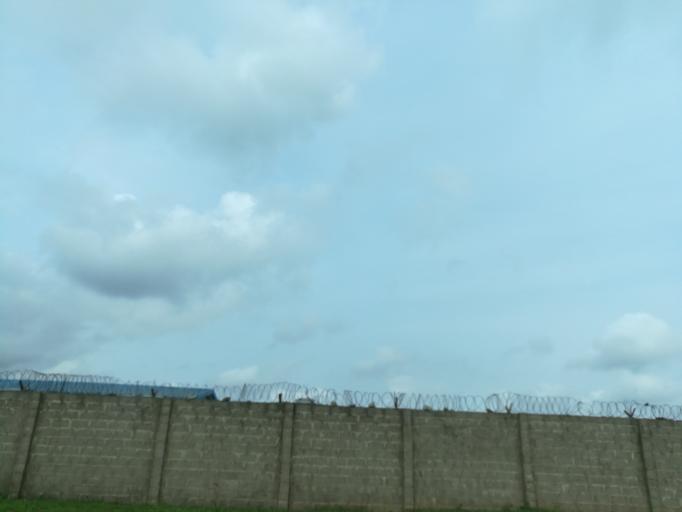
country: NG
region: Lagos
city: Oshodi
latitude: 6.5783
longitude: 3.3253
